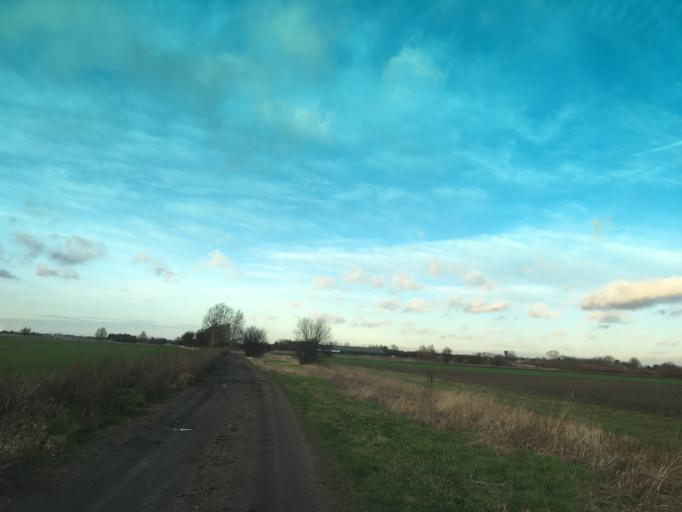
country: DK
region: Capital Region
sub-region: Tarnby Kommune
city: Tarnby
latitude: 55.5916
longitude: 12.6198
